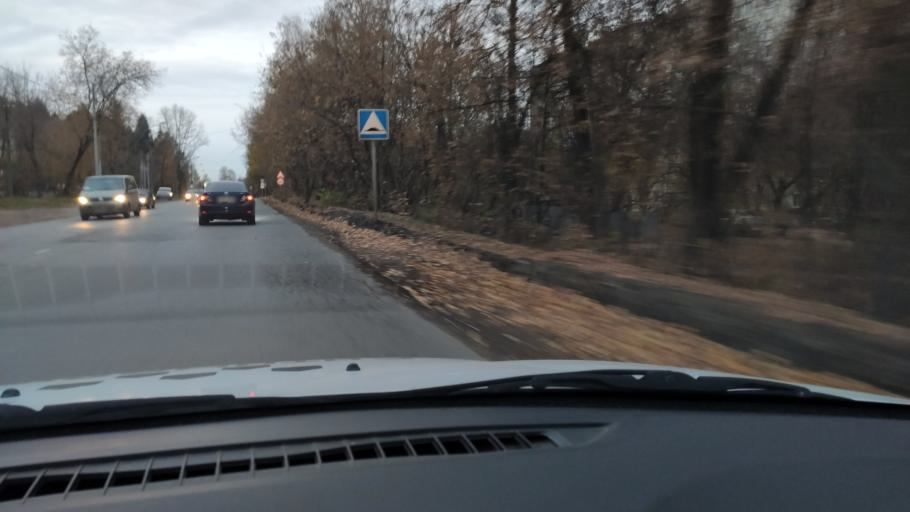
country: RU
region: Perm
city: Kondratovo
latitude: 58.0445
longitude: 56.0940
